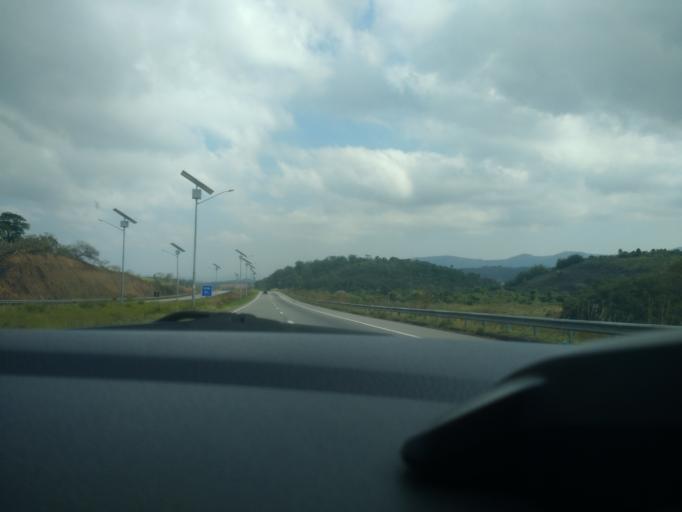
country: BR
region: Rio de Janeiro
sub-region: Queimados
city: Queimados
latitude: -22.6645
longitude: -43.5597
